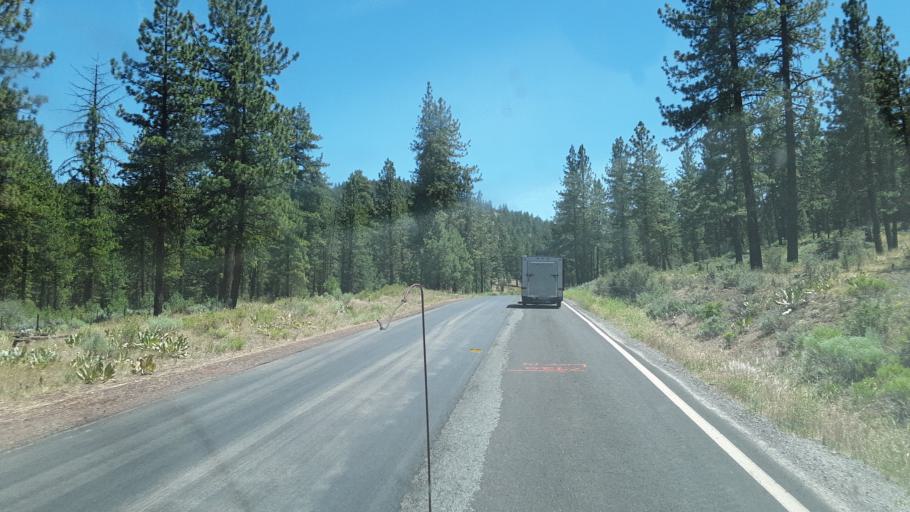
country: US
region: California
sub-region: Modoc County
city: Alturas
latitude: 40.9752
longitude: -120.7784
